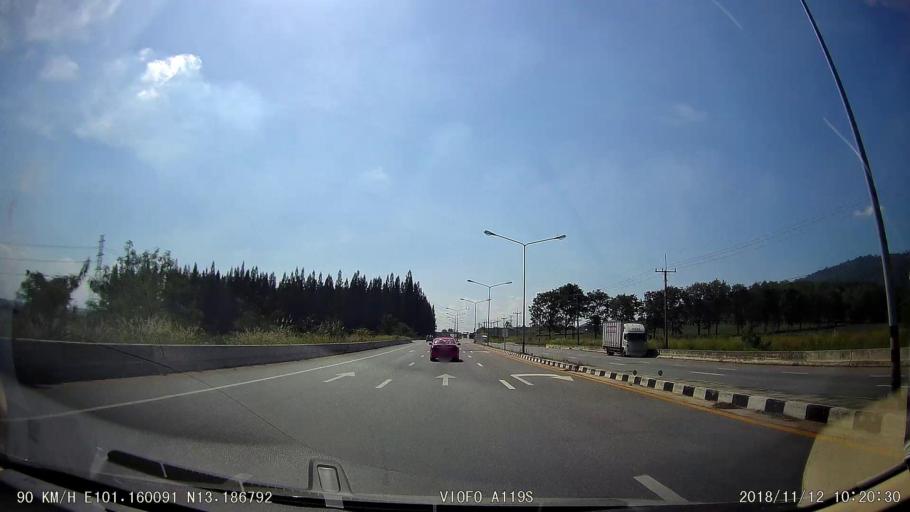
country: TH
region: Chon Buri
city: Ban Bueng
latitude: 13.1863
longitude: 101.1602
